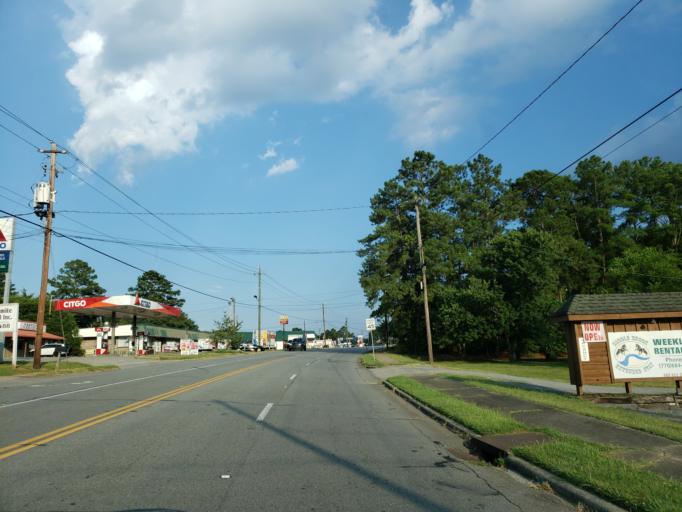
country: US
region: Georgia
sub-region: Polk County
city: Rockmart
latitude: 34.0051
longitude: -85.0647
